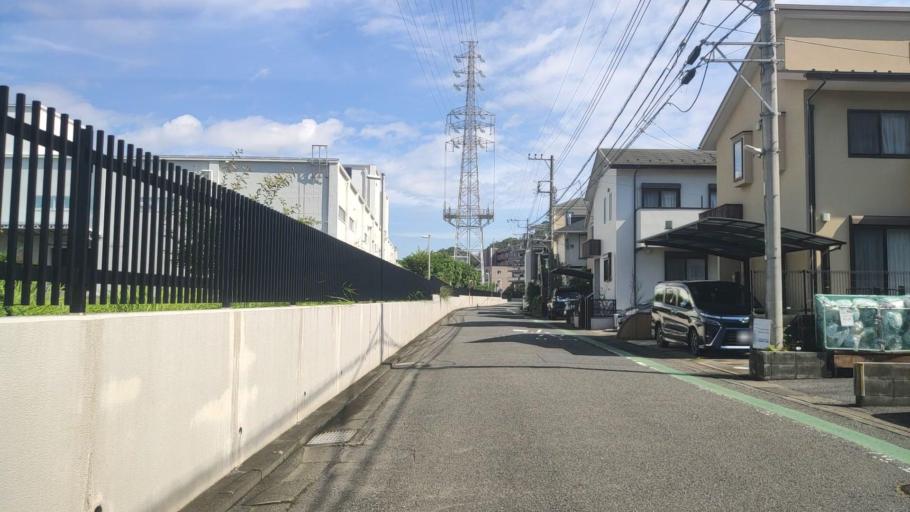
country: JP
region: Kanagawa
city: Kamakura
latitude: 35.3487
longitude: 139.5386
